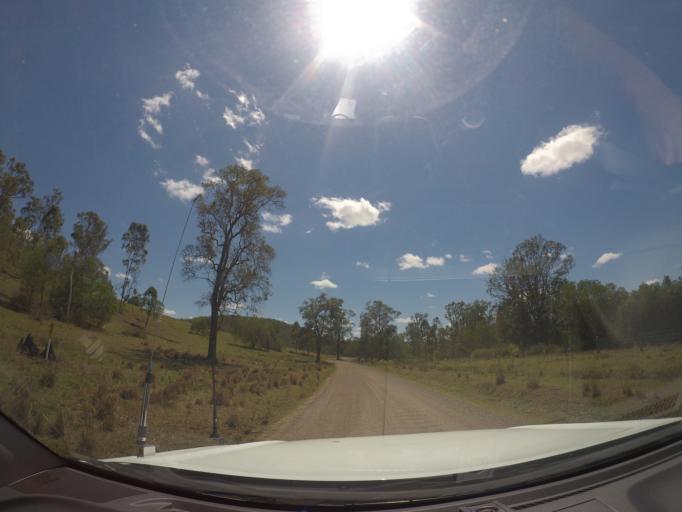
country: AU
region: Queensland
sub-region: Logan
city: Cedar Vale
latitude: -27.8642
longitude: 152.8531
